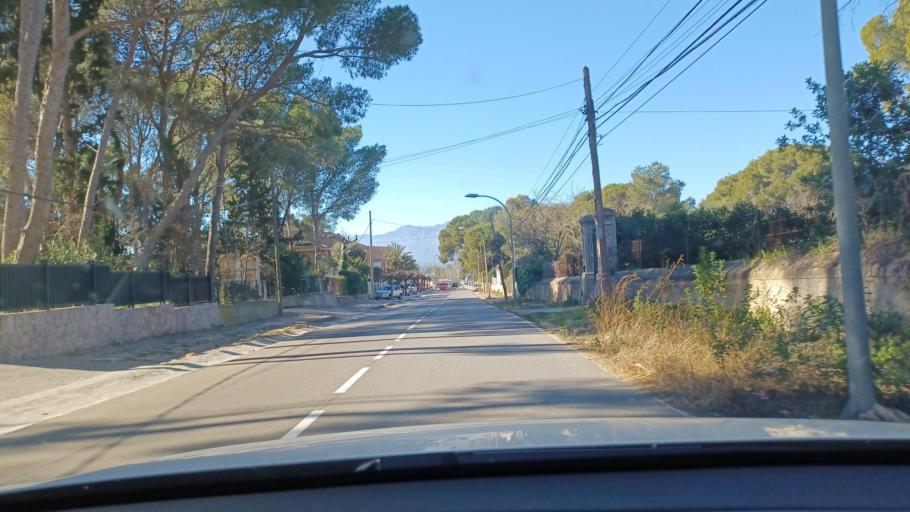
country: ES
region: Catalonia
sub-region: Provincia de Tarragona
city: Tortosa
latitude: 40.8127
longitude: 0.5321
